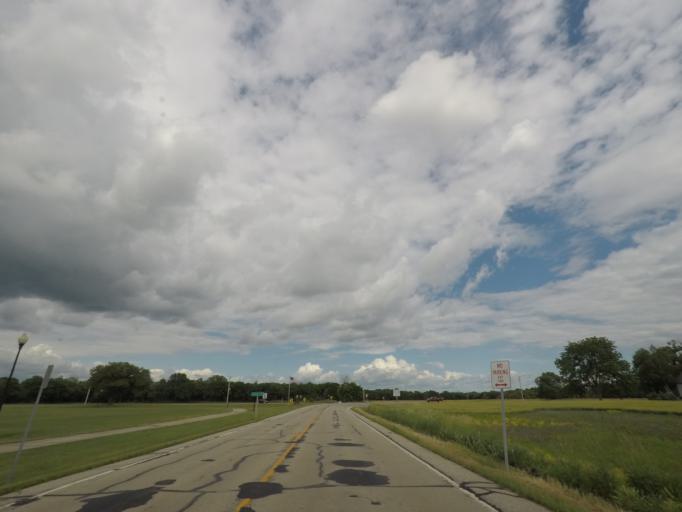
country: US
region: Wisconsin
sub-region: Dane County
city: Belleville
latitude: 42.8567
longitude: -89.5252
